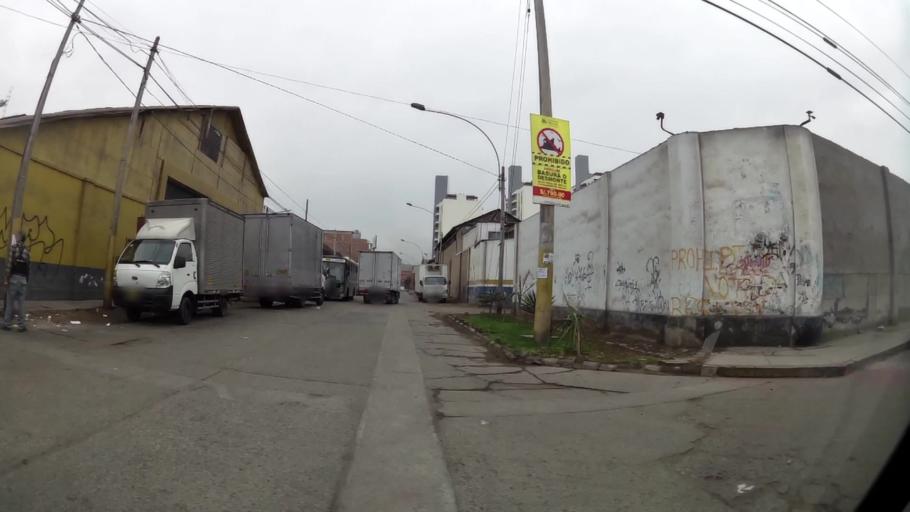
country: PE
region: Lima
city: Lima
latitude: -12.0518
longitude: -77.0539
